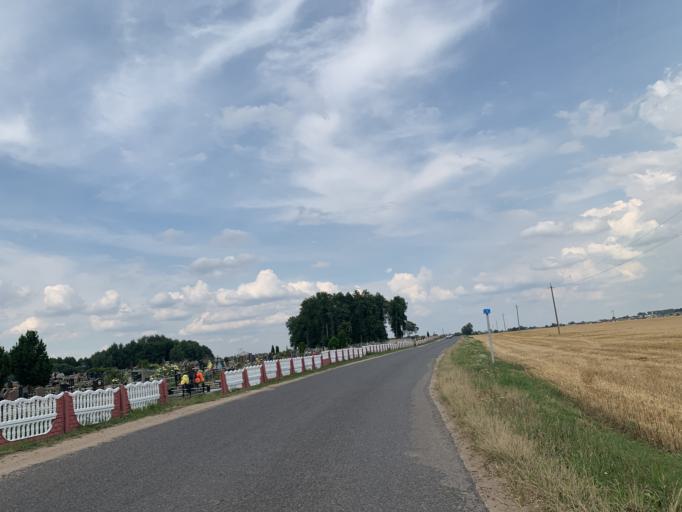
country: BY
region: Minsk
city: Nyasvizh
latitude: 53.1982
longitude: 26.6694
